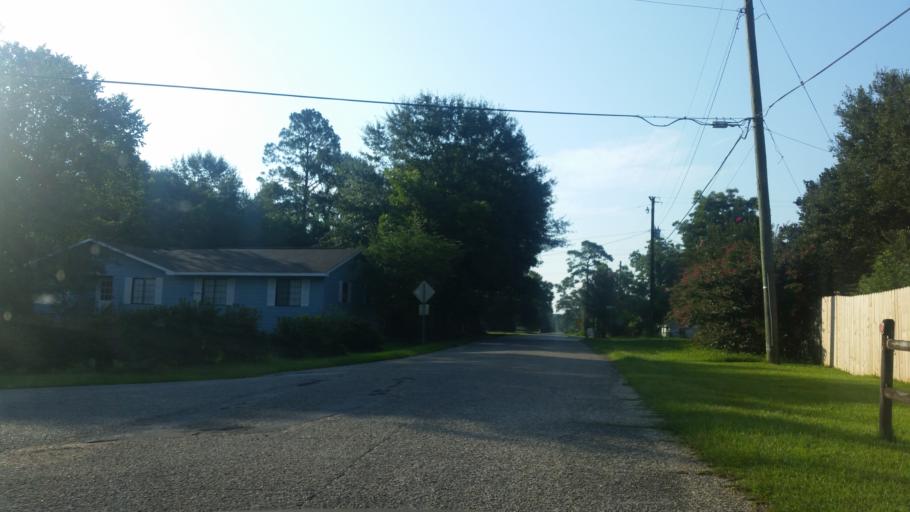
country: US
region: Florida
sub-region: Escambia County
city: Gonzalez
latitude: 30.5908
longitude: -87.3038
